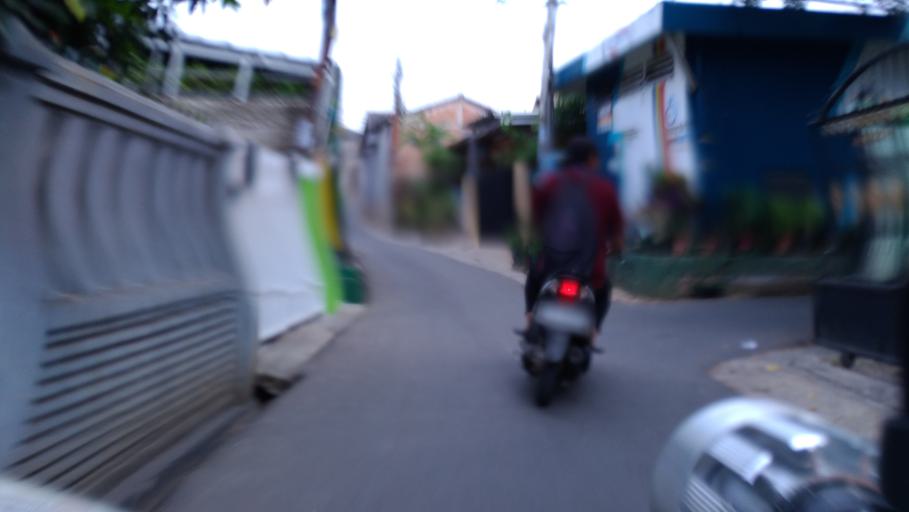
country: ID
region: West Java
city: Depok
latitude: -6.3550
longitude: 106.8715
